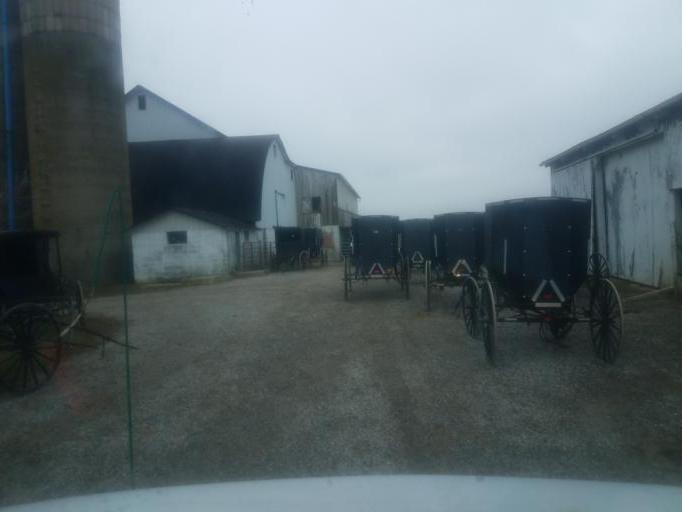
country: US
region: Ohio
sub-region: Huron County
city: Greenwich
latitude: 40.9075
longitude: -82.4530
